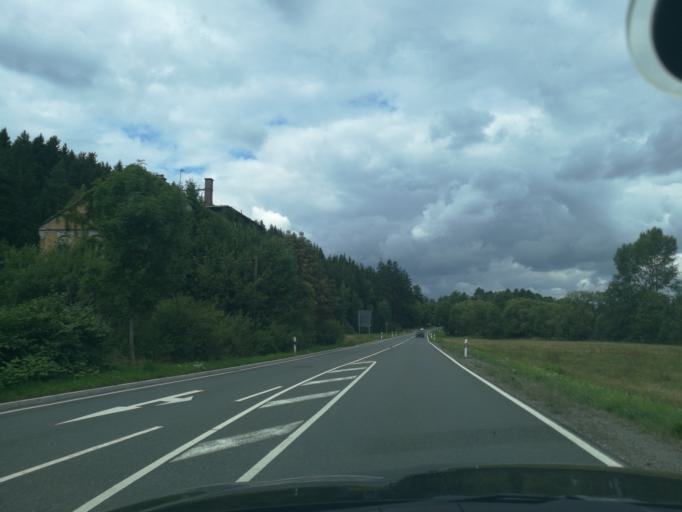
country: DE
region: Saxony
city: Adorf
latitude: 50.3441
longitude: 12.2408
